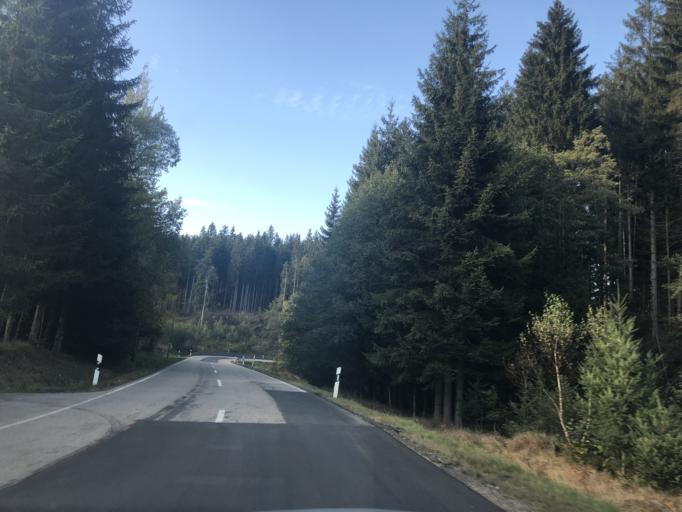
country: DE
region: Bavaria
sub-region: Lower Bavaria
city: Frauenau
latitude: 48.9760
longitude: 13.2992
